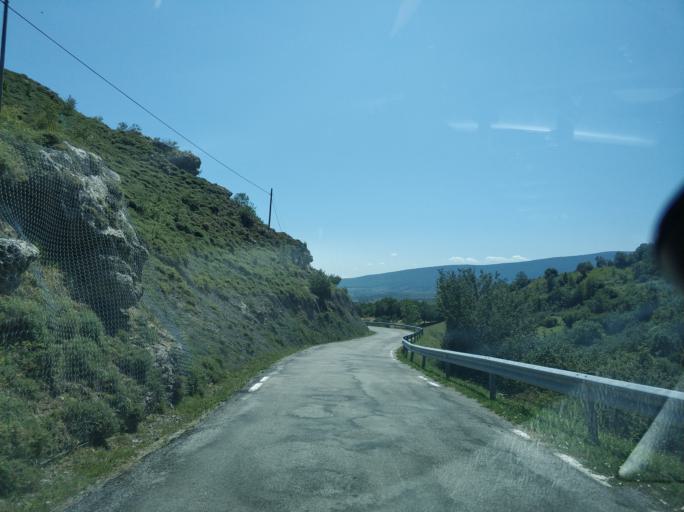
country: ES
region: Cantabria
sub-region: Provincia de Cantabria
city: Reinosa
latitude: 43.0262
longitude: -4.1690
